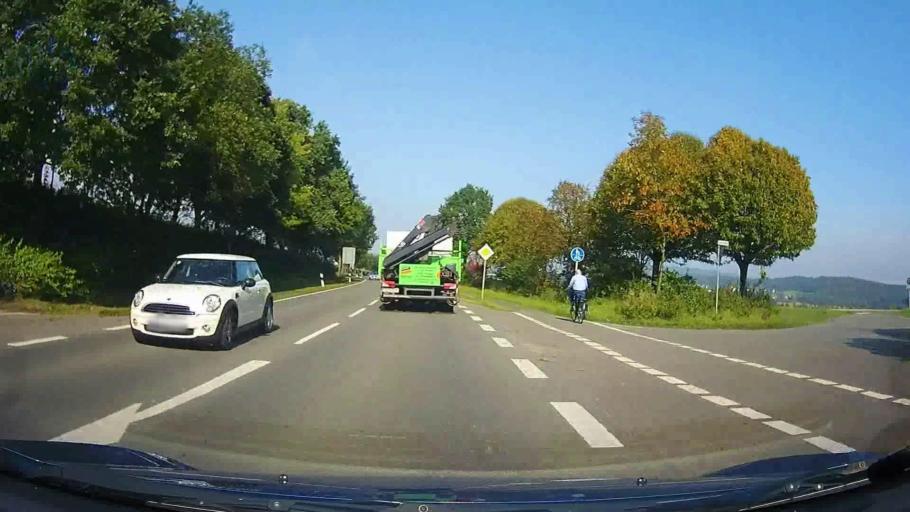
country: DE
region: Lower Saxony
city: Moringen
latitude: 51.6856
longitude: 9.8624
